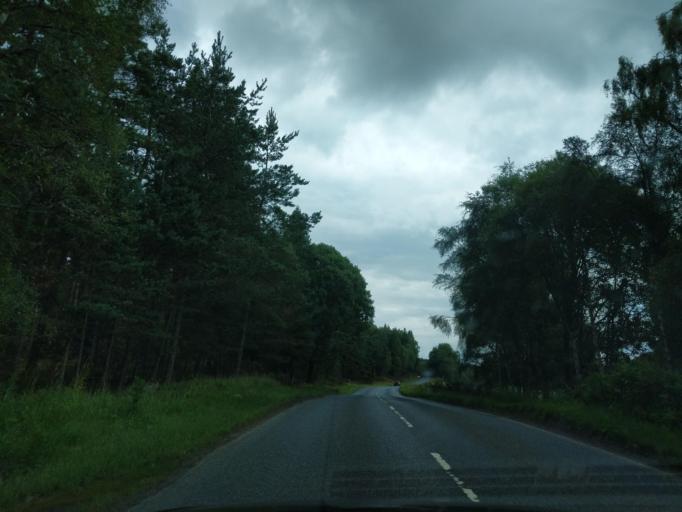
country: GB
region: Scotland
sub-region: Highland
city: Aviemore
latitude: 57.2920
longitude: -3.7915
